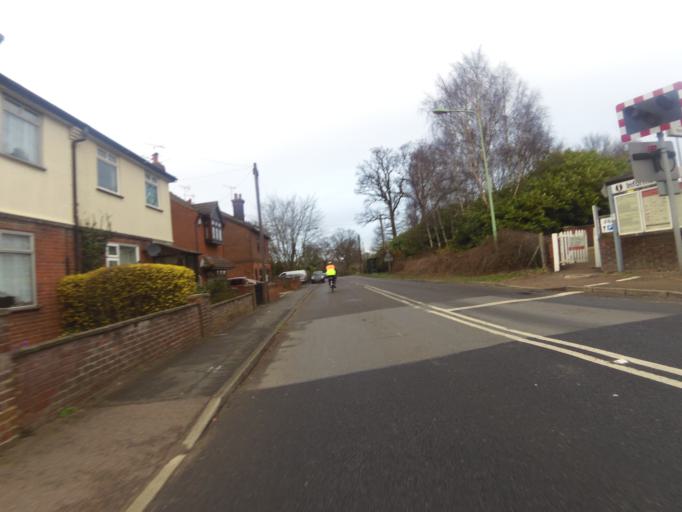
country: GB
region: England
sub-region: Suffolk
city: Ipswich
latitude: 52.0811
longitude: 1.1657
